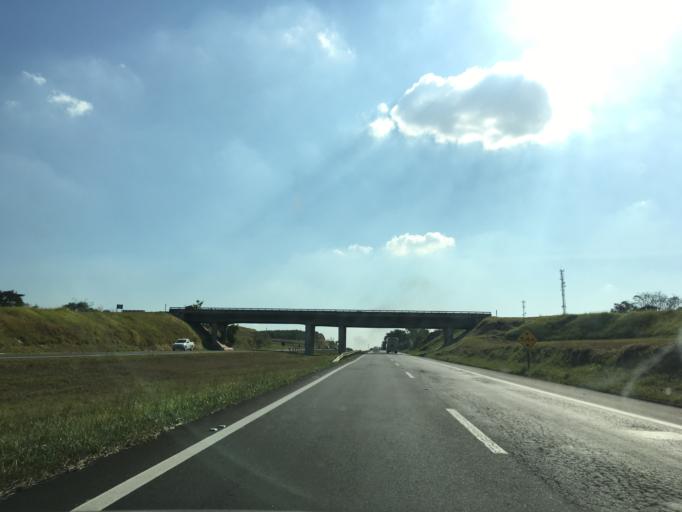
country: BR
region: Sao Paulo
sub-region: Santa Barbara D'Oeste
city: Santa Barbara d'Oeste
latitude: -22.7481
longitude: -47.5035
